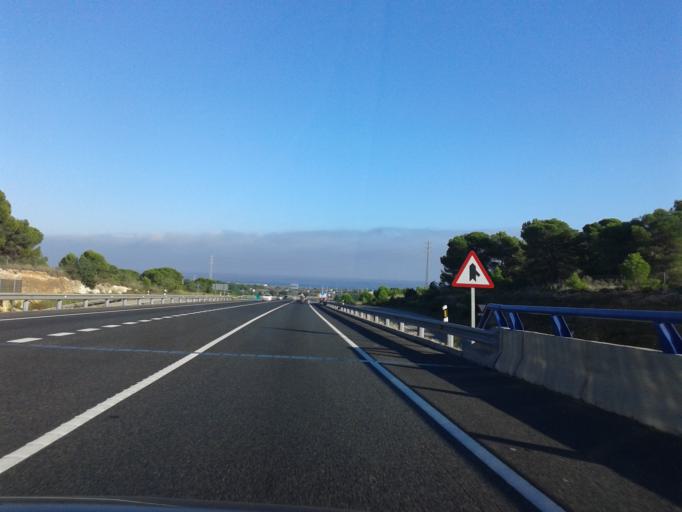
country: ES
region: Catalonia
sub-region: Provincia de Tarragona
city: Creixell
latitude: 41.1604
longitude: 1.4174
